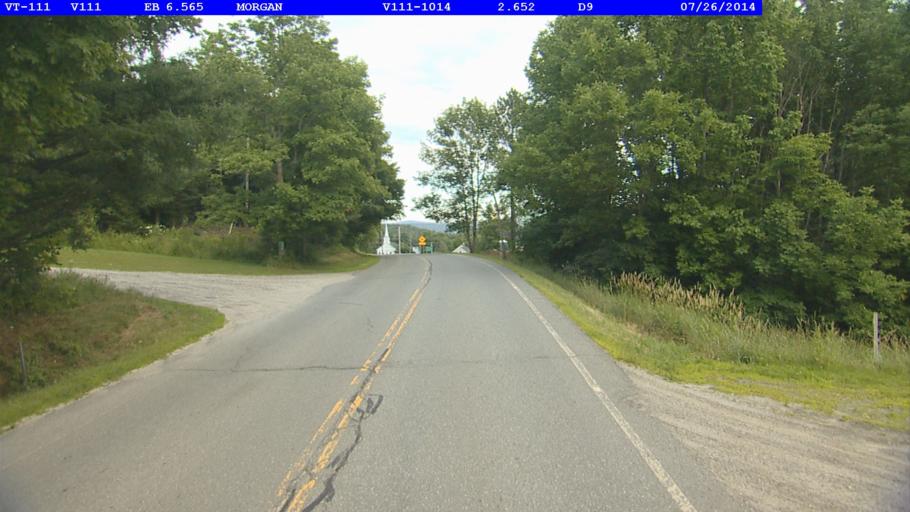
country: US
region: Vermont
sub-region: Orleans County
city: Newport
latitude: 44.9145
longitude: -72.0176
